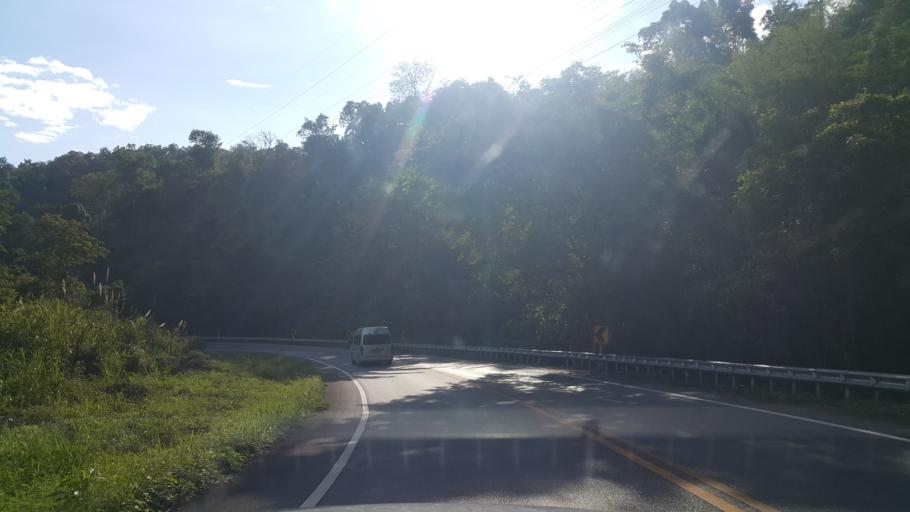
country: TH
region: Lampang
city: Wang Nuea
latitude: 19.0664
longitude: 99.7580
